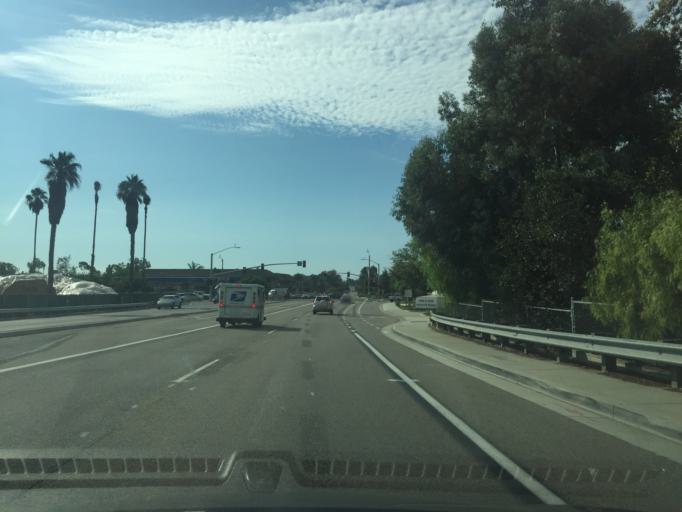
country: US
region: California
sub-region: Santa Barbara County
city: Isla Vista
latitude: 34.4316
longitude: -119.8698
